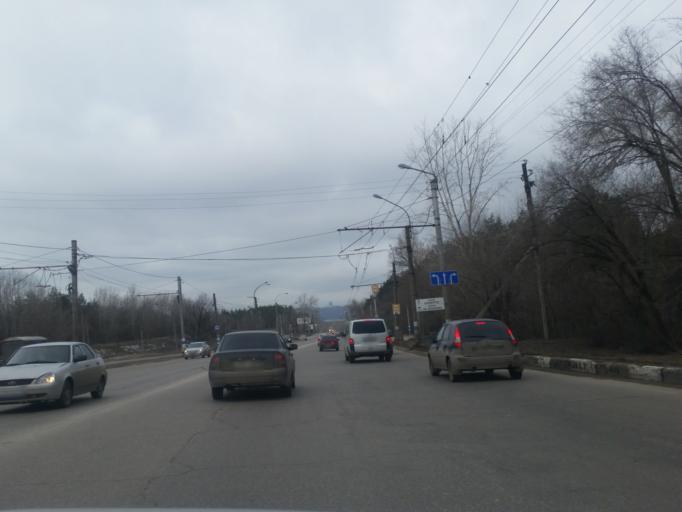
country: RU
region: Ulyanovsk
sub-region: Ulyanovskiy Rayon
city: Ulyanovsk
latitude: 54.3347
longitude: 48.5232
